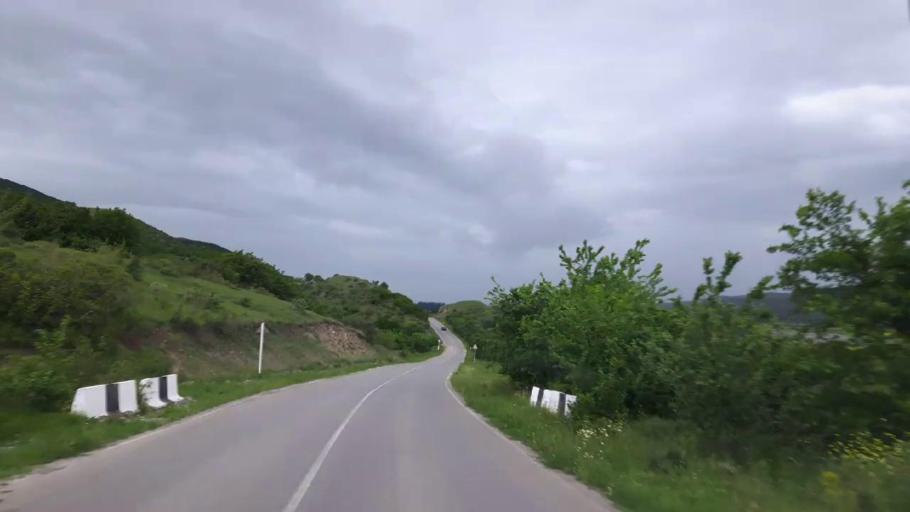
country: GE
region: Shida Kartli
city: Gori
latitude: 41.9881
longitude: 44.0433
